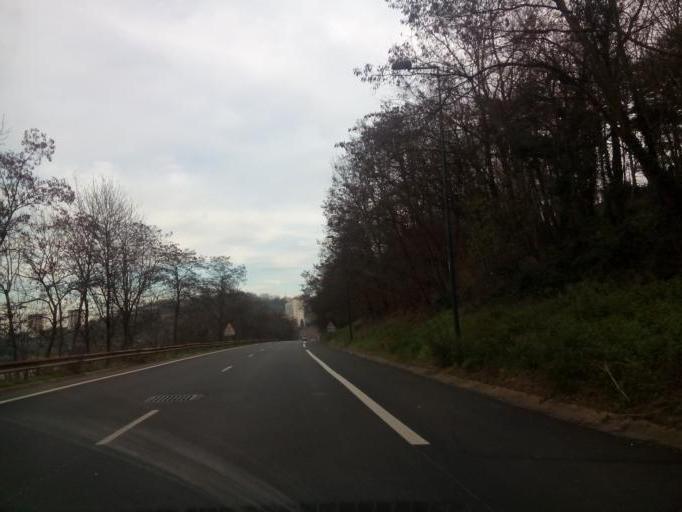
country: FR
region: Rhone-Alpes
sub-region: Departement du Rhone
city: Tassin-la-Demi-Lune
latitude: 45.7660
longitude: 4.7921
